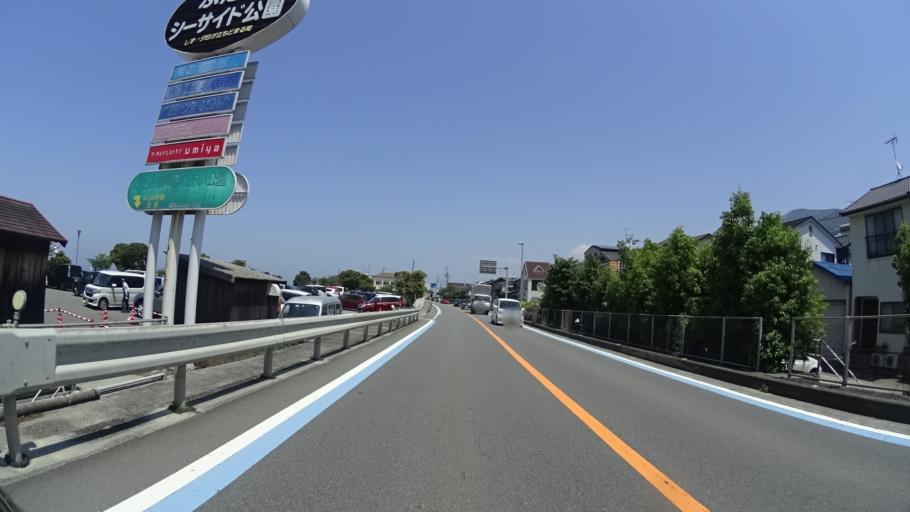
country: JP
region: Ehime
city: Iyo
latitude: 33.6864
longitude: 132.6357
